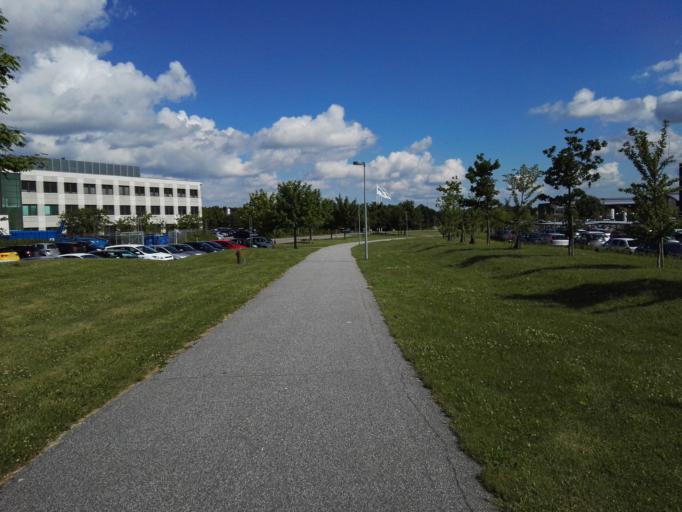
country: DK
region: Capital Region
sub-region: Ballerup Kommune
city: Ballerup
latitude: 55.7376
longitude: 12.3876
